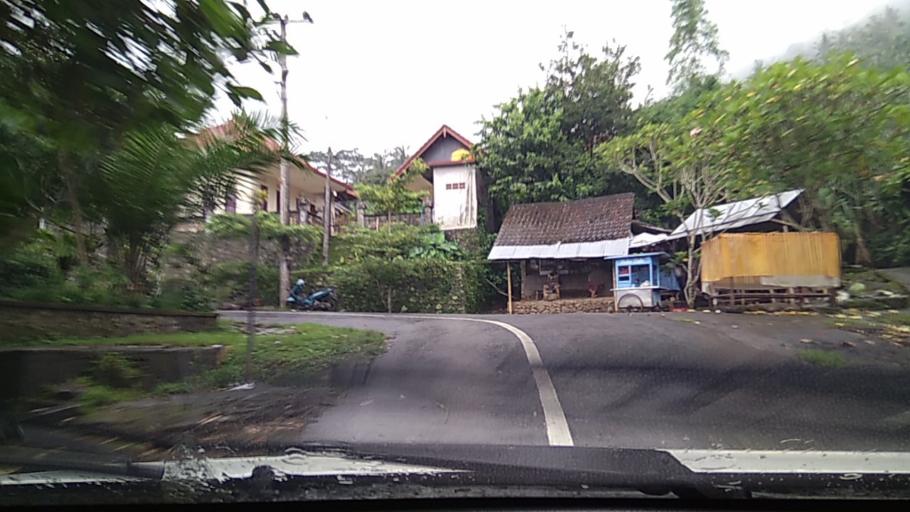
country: ID
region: Bali
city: Tiyingtali Kelod
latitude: -8.4079
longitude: 115.6266
